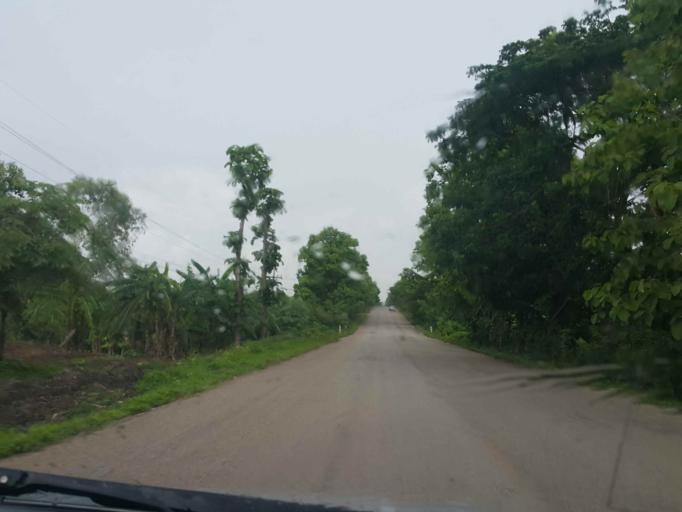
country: TH
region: Phayao
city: Dok Kham Tai
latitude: 19.0126
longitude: 100.0622
